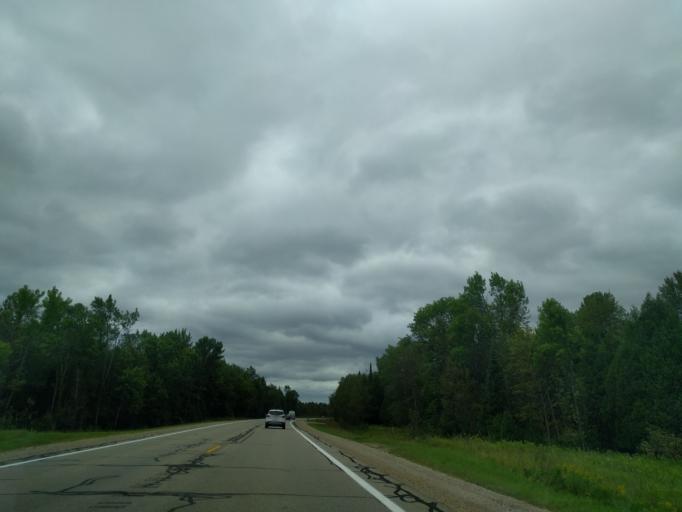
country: US
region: Michigan
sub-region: Menominee County
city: Menominee
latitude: 45.3595
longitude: -87.3994
